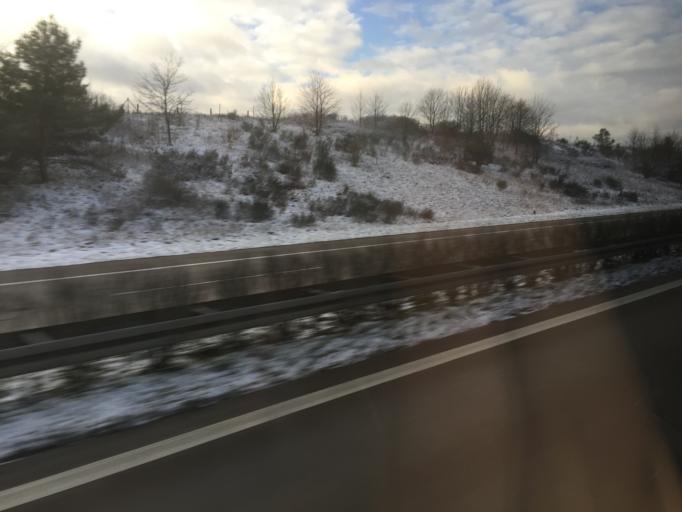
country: DE
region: Mecklenburg-Vorpommern
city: Siggelkow
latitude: 53.3146
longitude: 11.9009
